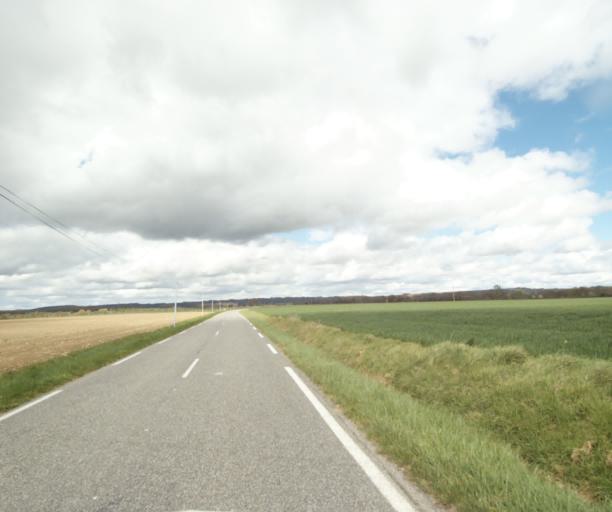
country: FR
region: Midi-Pyrenees
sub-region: Departement de la Haute-Garonne
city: Calmont
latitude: 43.2476
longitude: 1.6367
